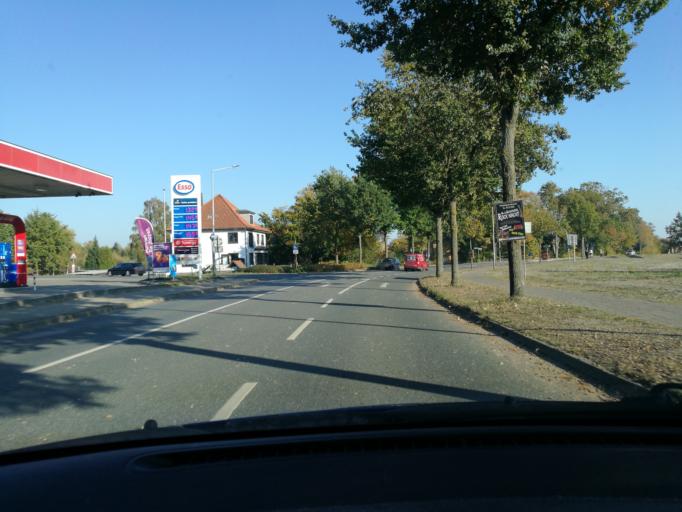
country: DE
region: Lower Saxony
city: Dannenberg
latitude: 53.1029
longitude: 11.1068
